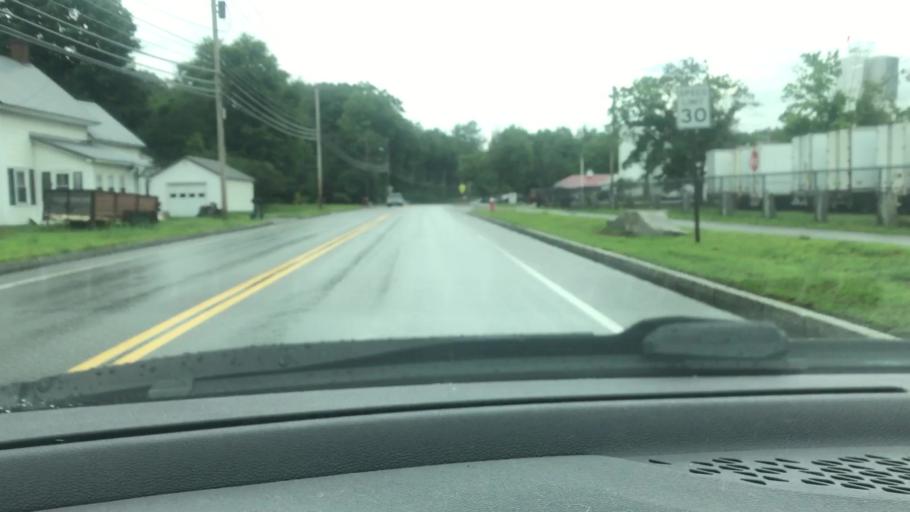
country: US
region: New Hampshire
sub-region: Merrimack County
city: East Concord
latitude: 43.2325
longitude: -71.5606
